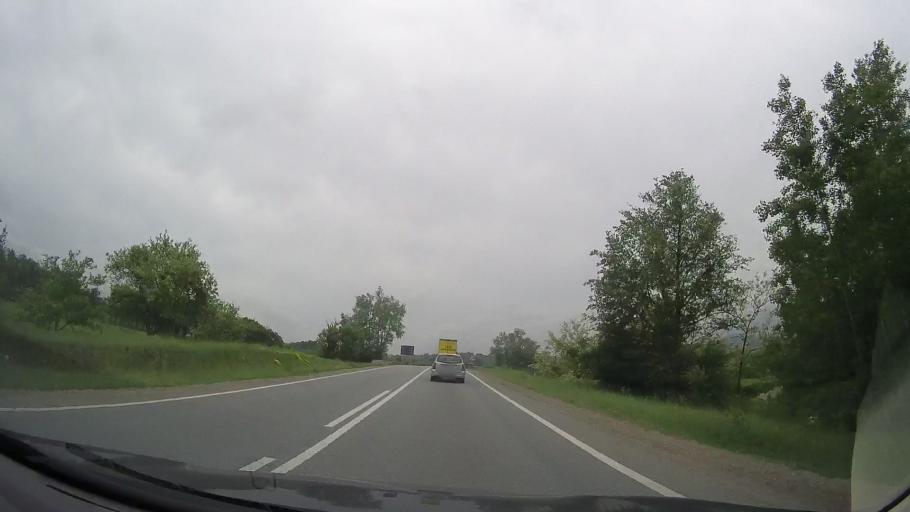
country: RO
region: Caras-Severin
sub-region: Comuna Teregova
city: Teregova
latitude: 45.1633
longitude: 22.3041
